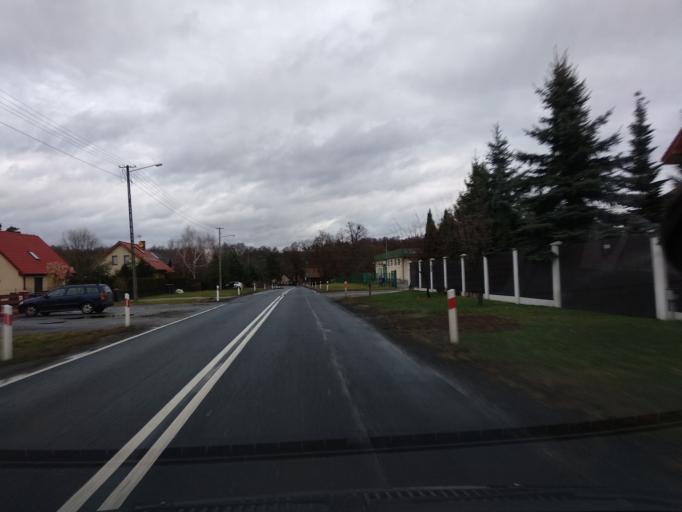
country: PL
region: Lower Silesian Voivodeship
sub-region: Powiat olesnicki
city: Olesnica
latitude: 51.2468
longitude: 17.4730
